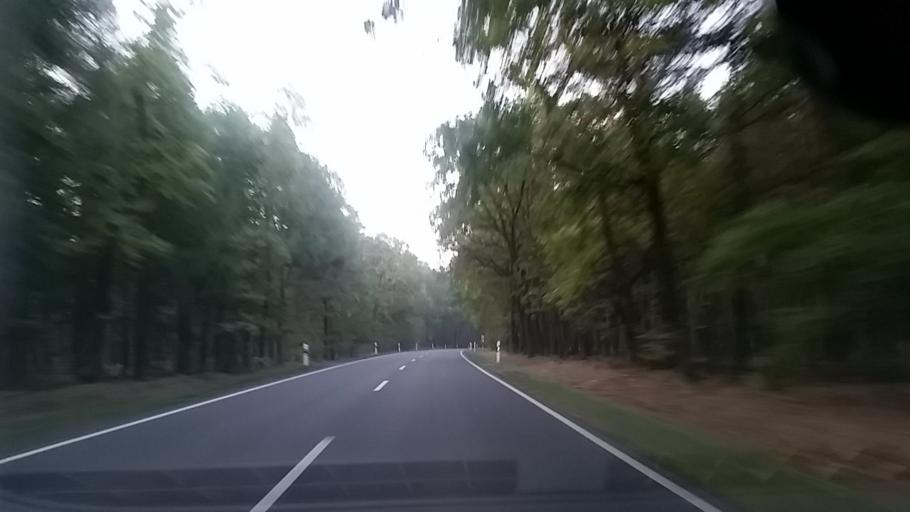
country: DE
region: Lower Saxony
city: Luder
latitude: 52.7841
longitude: 10.7157
